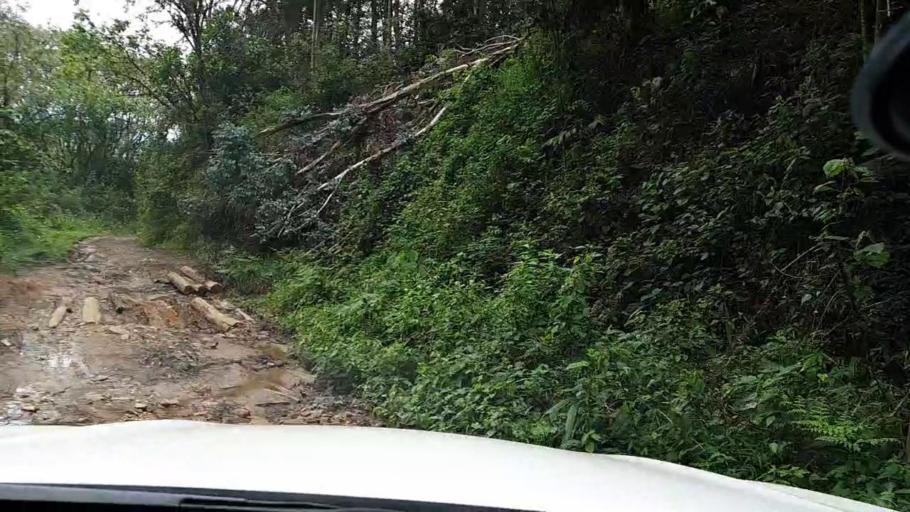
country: RW
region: Western Province
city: Kibuye
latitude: -2.2796
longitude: 29.3056
